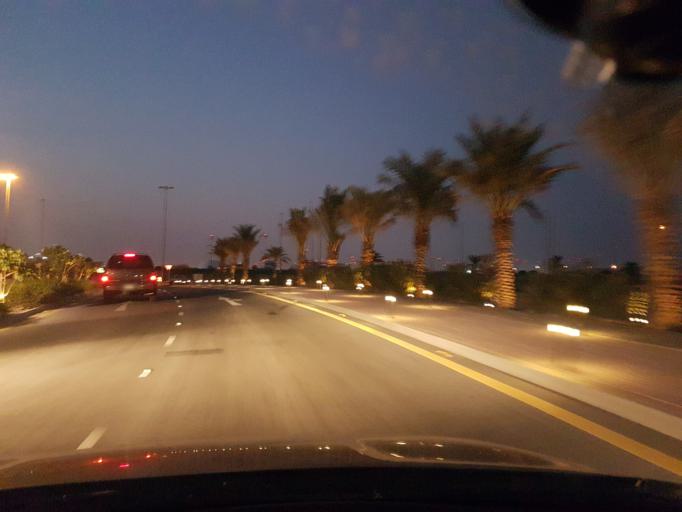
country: BH
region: Central Governorate
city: Dar Kulayb
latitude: 26.0194
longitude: 50.5097
